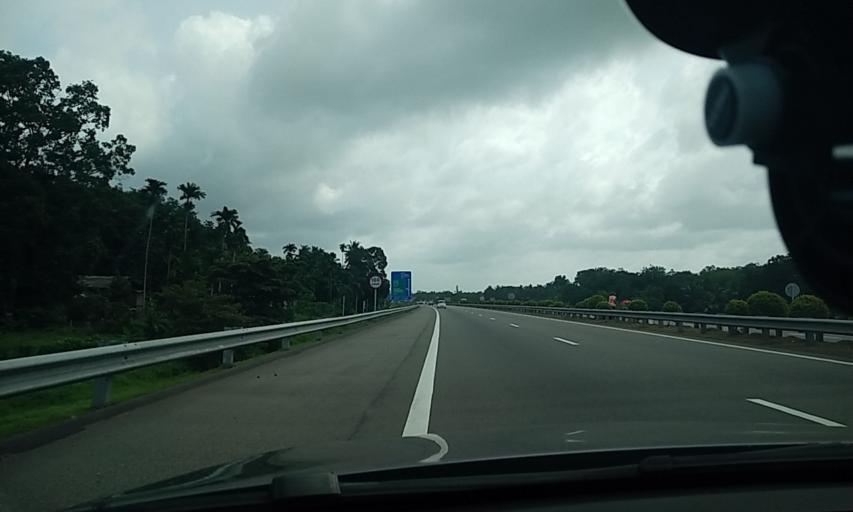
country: LK
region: Western
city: Homagama
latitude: 6.8671
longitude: 79.9783
